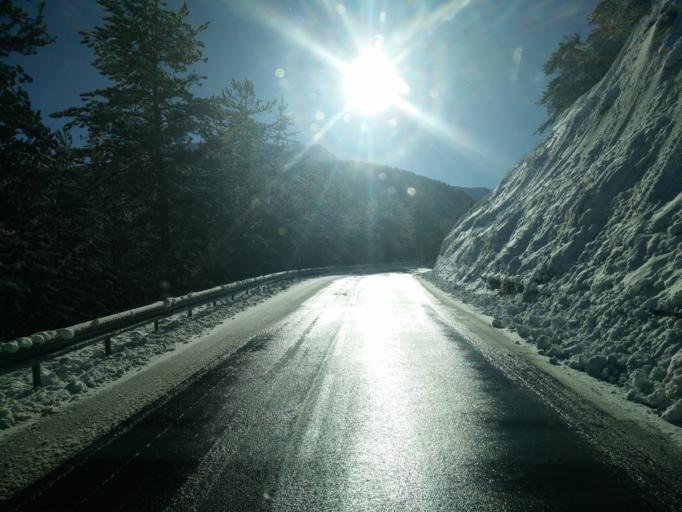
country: FR
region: Provence-Alpes-Cote d'Azur
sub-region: Departement des Alpes-de-Haute-Provence
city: Annot
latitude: 43.9211
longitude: 6.6138
